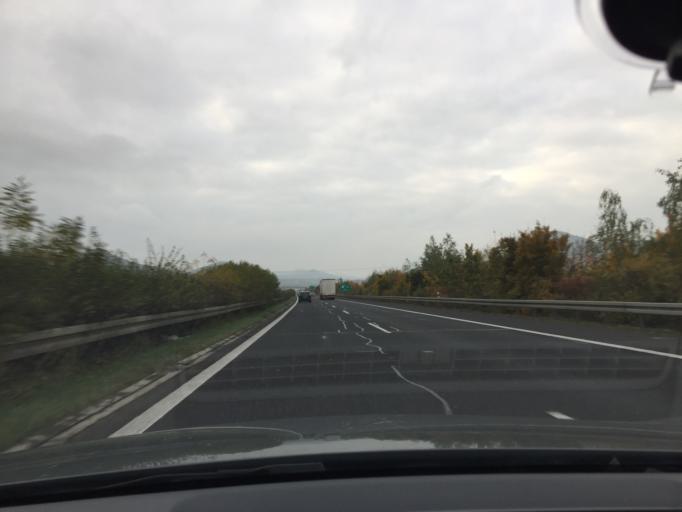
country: CZ
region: Ustecky
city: Lovosice
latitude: 50.5028
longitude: 14.0562
